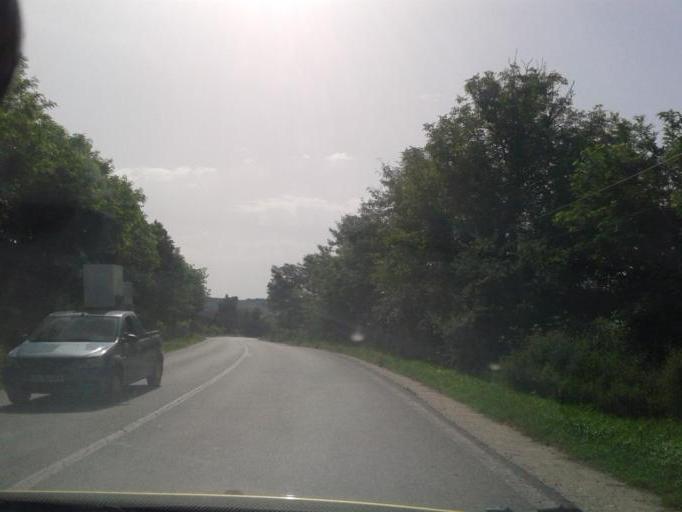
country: RO
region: Valcea
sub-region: Comuna Bunesti
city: Bunesti
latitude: 45.1107
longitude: 24.1817
